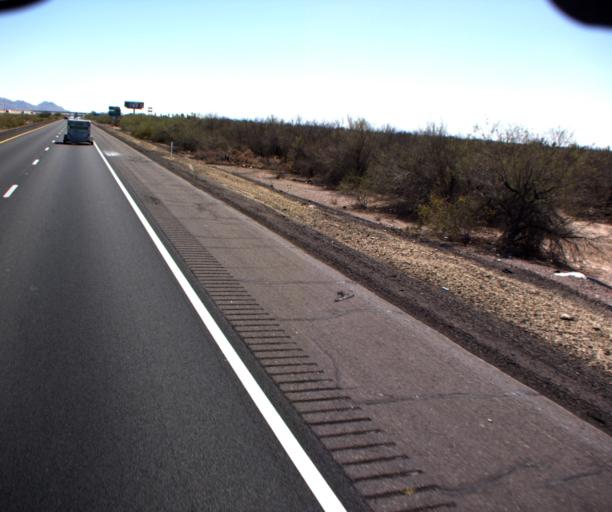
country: US
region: Arizona
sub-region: La Paz County
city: Salome
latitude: 33.6328
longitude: -113.7816
